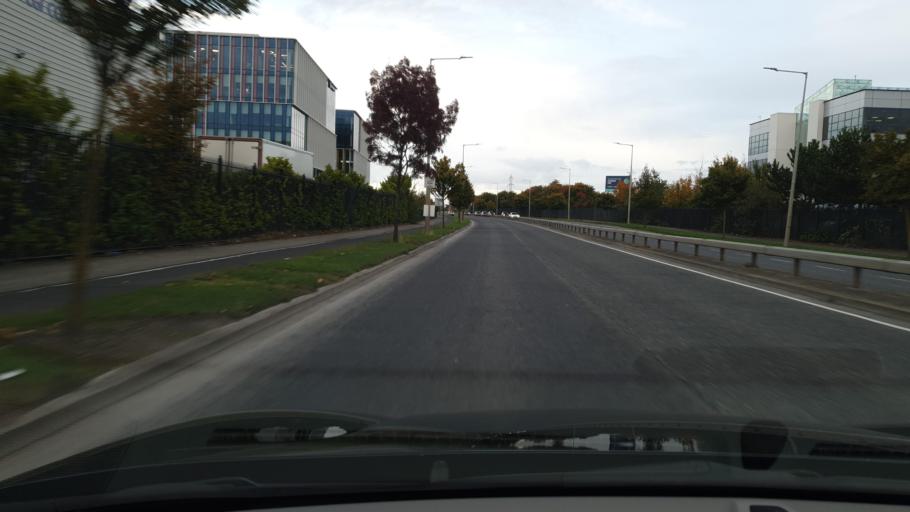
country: IE
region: Leinster
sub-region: Fingal County
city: Blanchardstown
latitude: 53.4123
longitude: -6.3670
